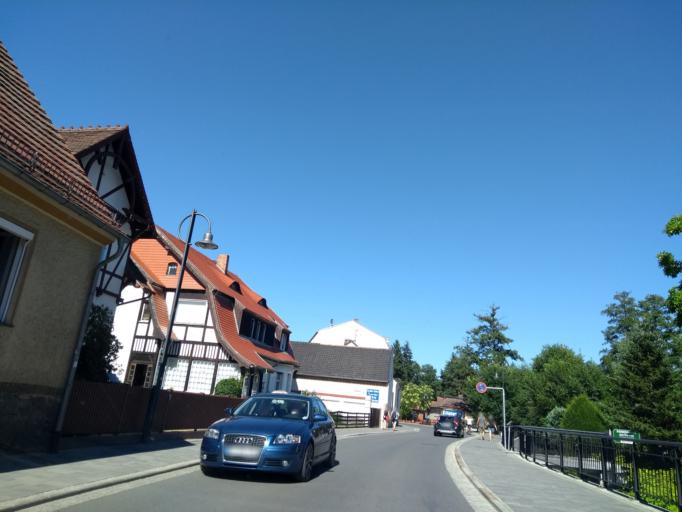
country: DE
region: Brandenburg
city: Lubbenau
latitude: 51.8647
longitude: 13.9723
